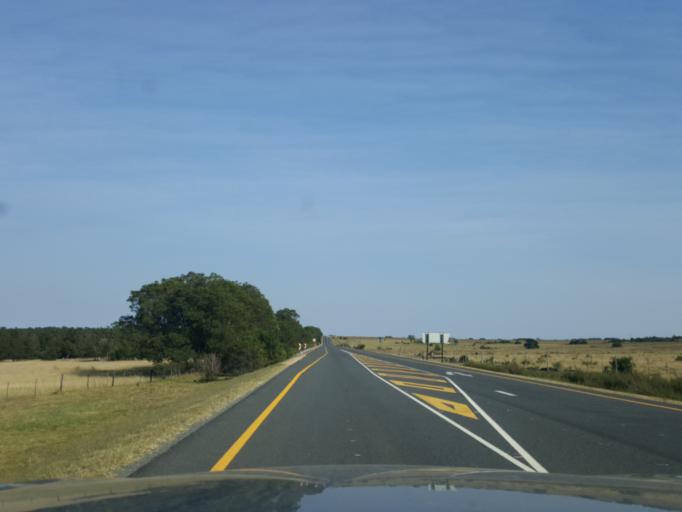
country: ZA
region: Eastern Cape
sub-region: Cacadu District Municipality
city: Grahamstown
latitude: -33.4318
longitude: 26.3219
